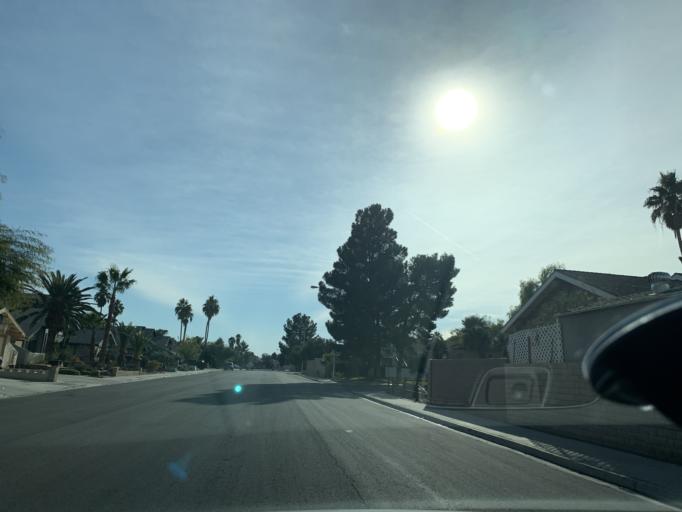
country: US
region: Nevada
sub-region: Clark County
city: Spring Valley
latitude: 36.1063
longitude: -115.2346
